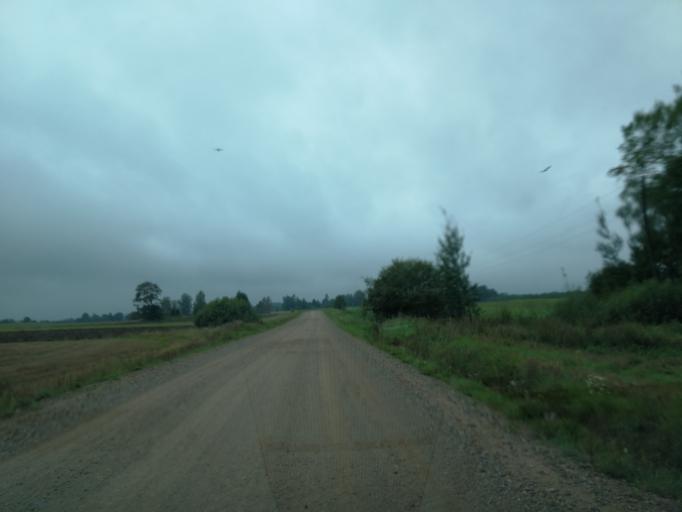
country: LV
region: Vilanu
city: Vilani
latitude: 56.3731
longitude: 27.0393
